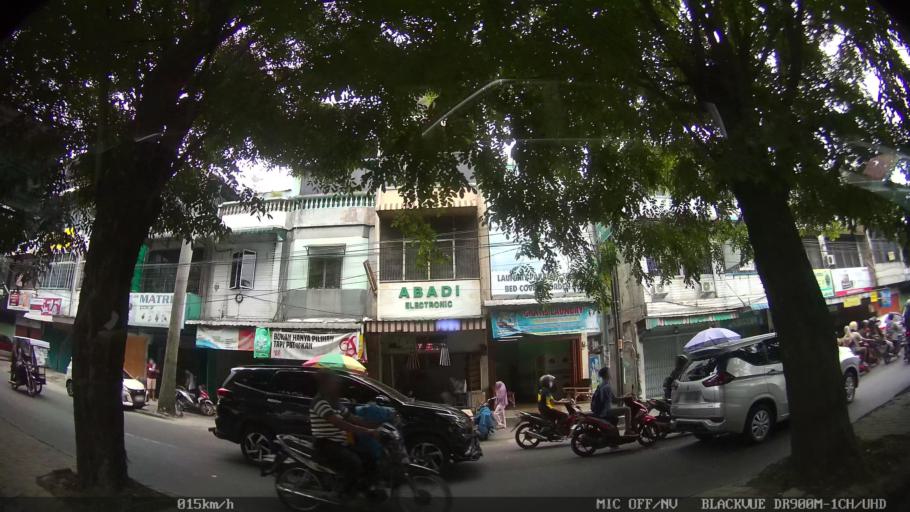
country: ID
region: North Sumatra
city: Medan
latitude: 3.5527
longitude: 98.6886
